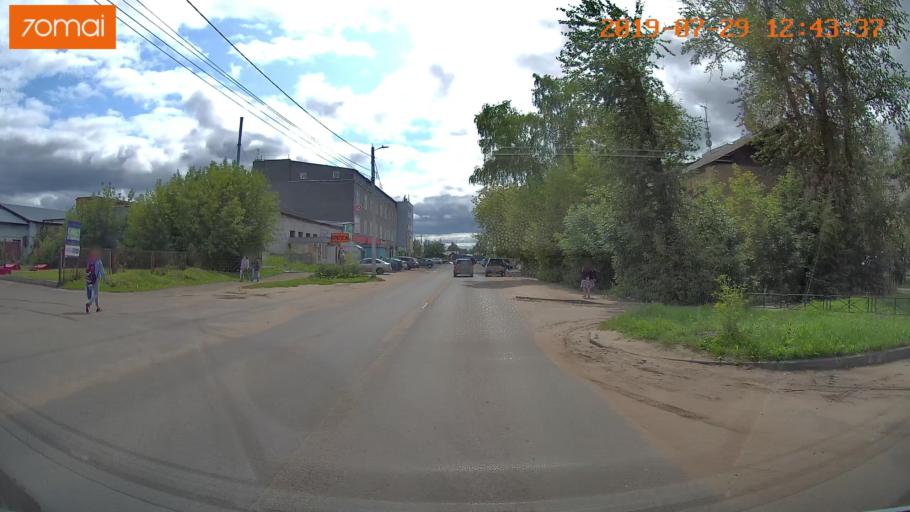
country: RU
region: Ivanovo
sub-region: Gorod Ivanovo
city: Ivanovo
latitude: 57.0013
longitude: 40.9305
